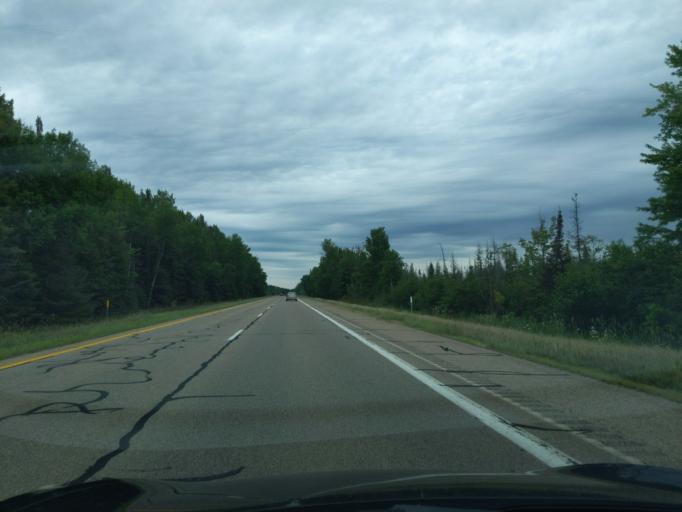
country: US
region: Michigan
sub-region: Roscommon County
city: Houghton Lake
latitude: 44.2925
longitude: -84.8011
